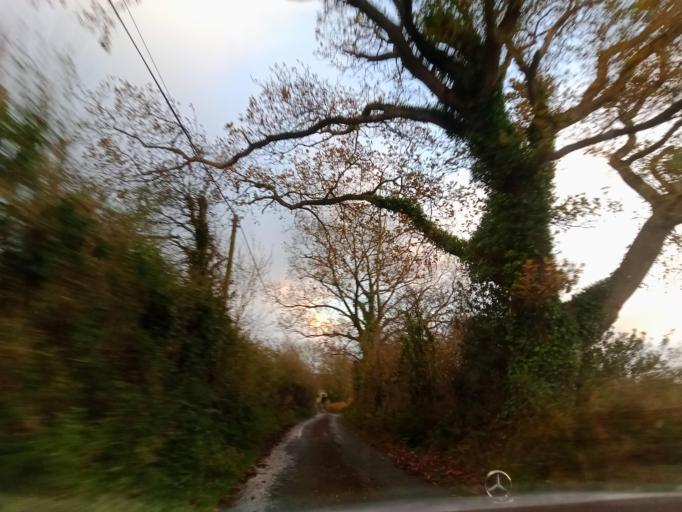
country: IE
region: Leinster
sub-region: Loch Garman
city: New Ross
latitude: 52.3378
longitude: -7.0104
